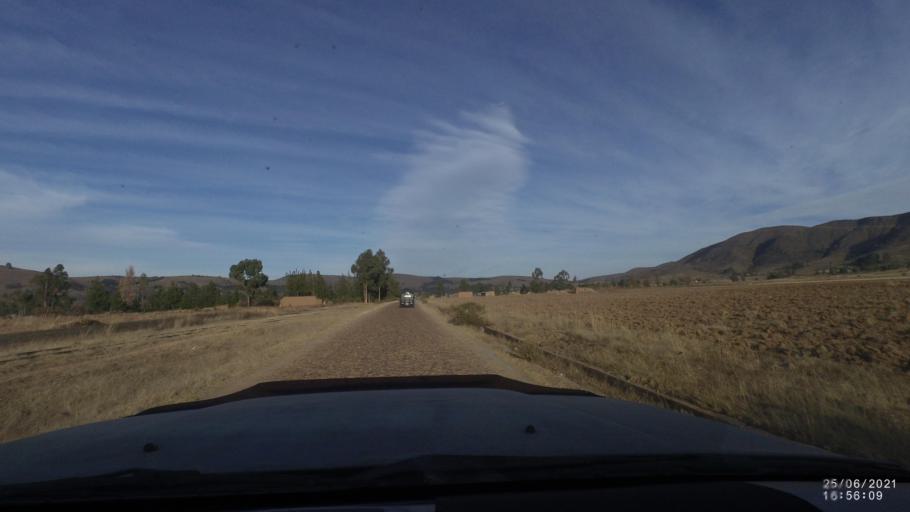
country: BO
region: Cochabamba
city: Arani
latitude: -17.8239
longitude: -65.7694
